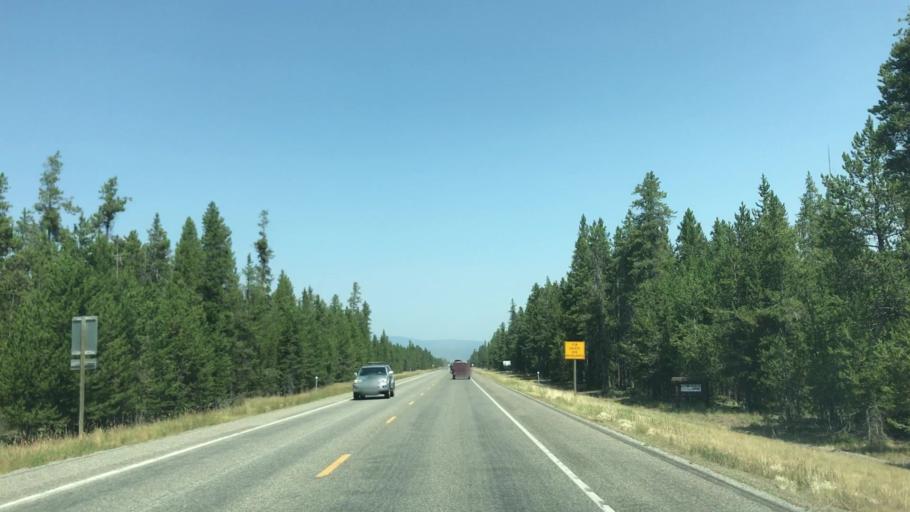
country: US
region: Montana
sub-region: Gallatin County
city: West Yellowstone
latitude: 44.6778
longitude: -111.1006
